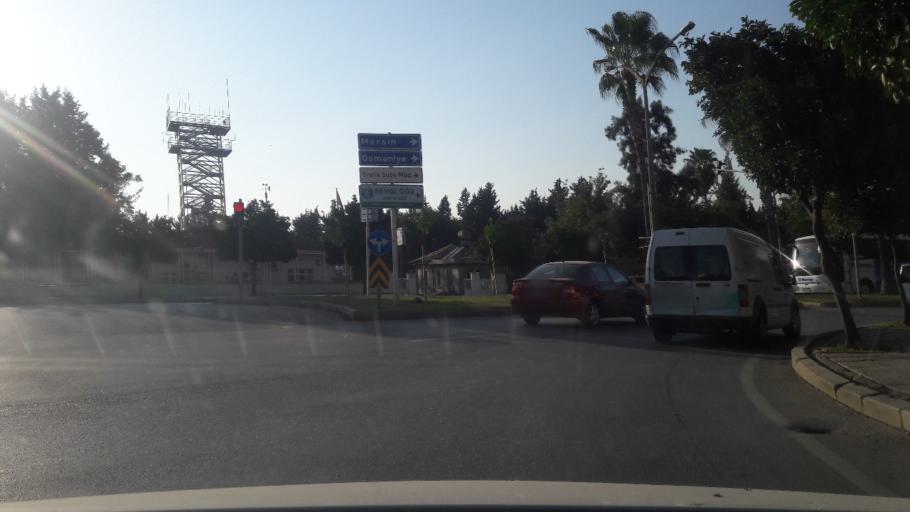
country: TR
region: Adana
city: Seyhan
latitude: 36.9875
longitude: 35.2982
